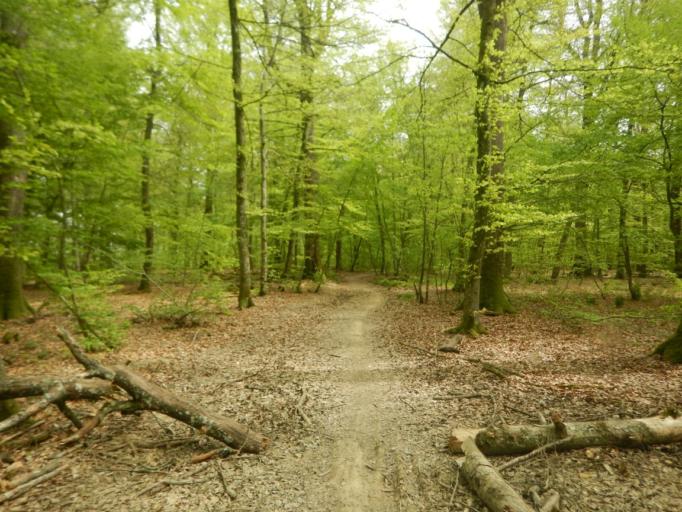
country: LU
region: Grevenmacher
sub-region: Canton d'Echternach
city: Consdorf
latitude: 49.7641
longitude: 6.3405
